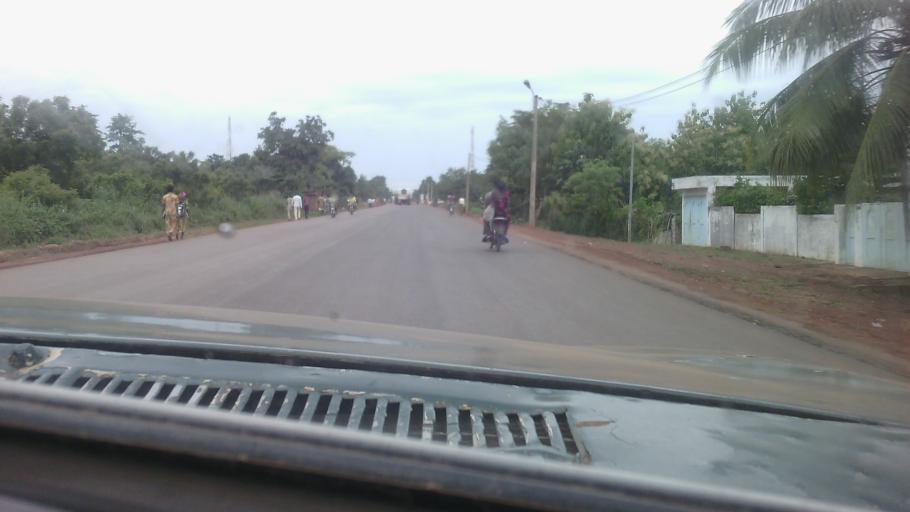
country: BJ
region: Mono
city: Come
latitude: 6.5233
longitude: 1.8194
